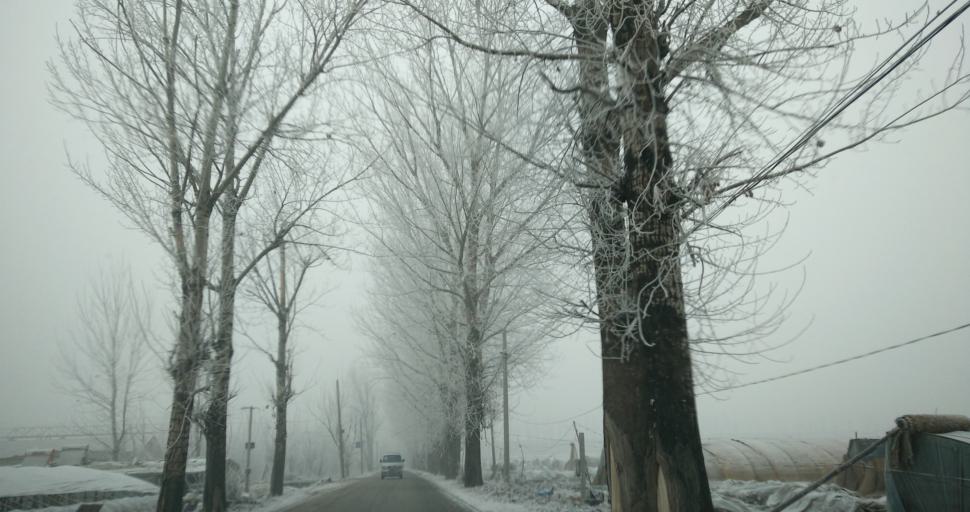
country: CN
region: Beijing
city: Yinghai
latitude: 39.7063
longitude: 116.4290
